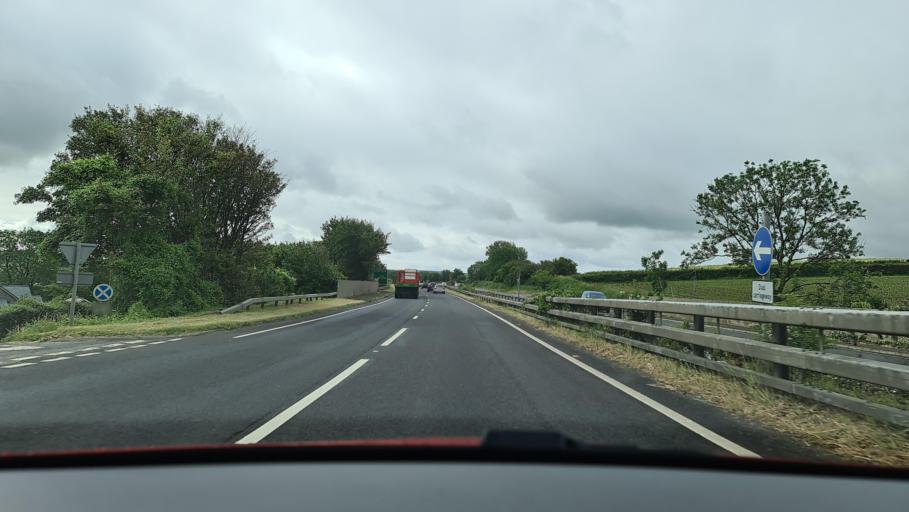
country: GB
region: England
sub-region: Cornwall
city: Liskeard
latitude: 50.4361
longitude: -4.4400
